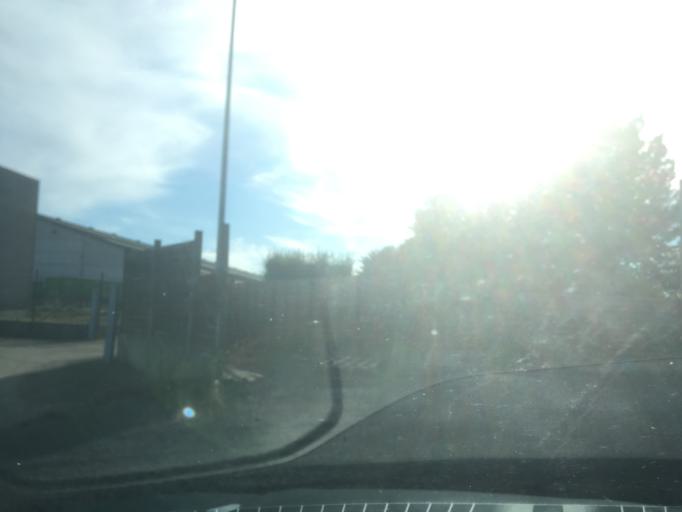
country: BE
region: Flanders
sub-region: Provincie West-Vlaanderen
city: Izegem
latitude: 50.9221
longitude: 3.1857
